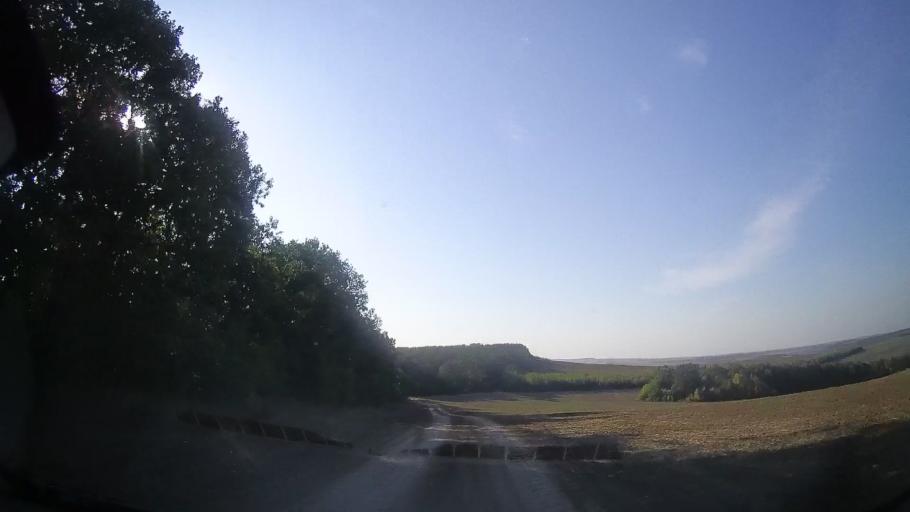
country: RO
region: Timis
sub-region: Comuna Bogda
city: Bogda
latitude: 45.9192
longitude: 21.6118
